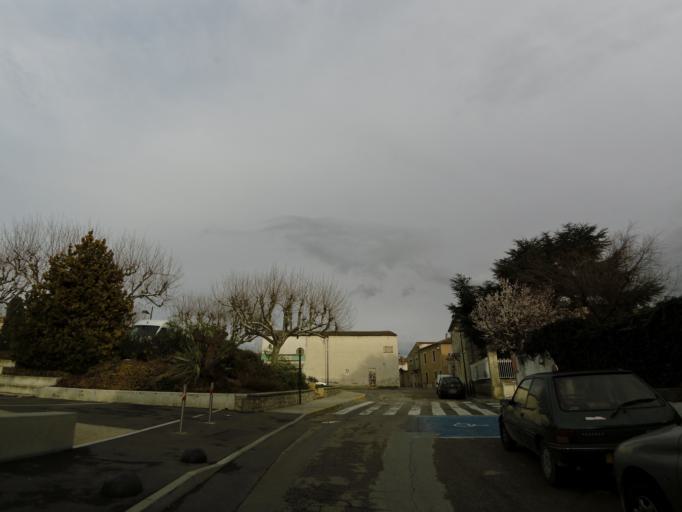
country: FR
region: Languedoc-Roussillon
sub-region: Departement du Gard
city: Vergeze
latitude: 43.7422
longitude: 4.2201
